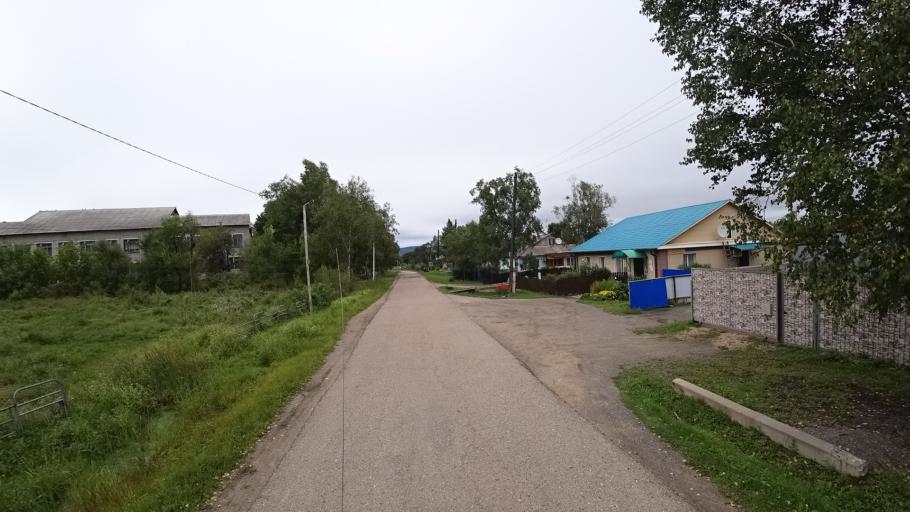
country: RU
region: Primorskiy
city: Monastyrishche
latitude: 44.0822
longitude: 132.5819
